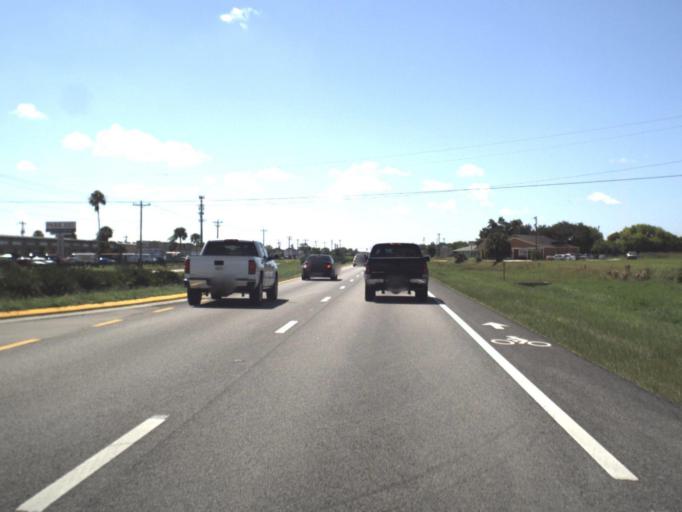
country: US
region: Florida
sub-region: Lee County
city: Lochmoor Waterway Estates
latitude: 26.6634
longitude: -81.9503
